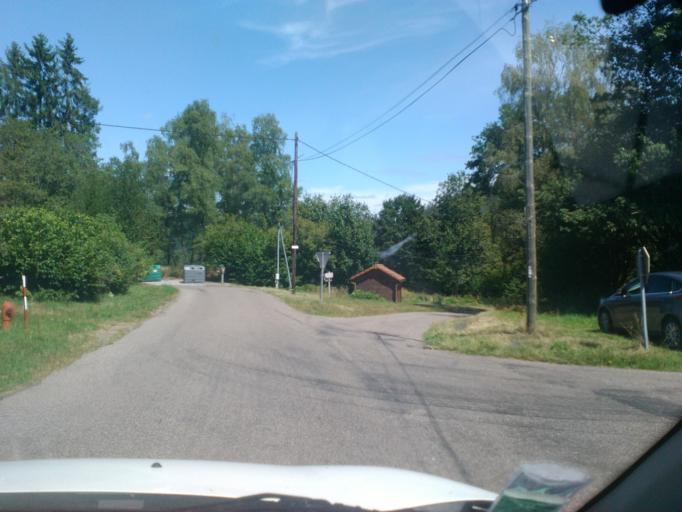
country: FR
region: Lorraine
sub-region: Departement des Vosges
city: Le Tholy
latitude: 48.0730
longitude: 6.7523
